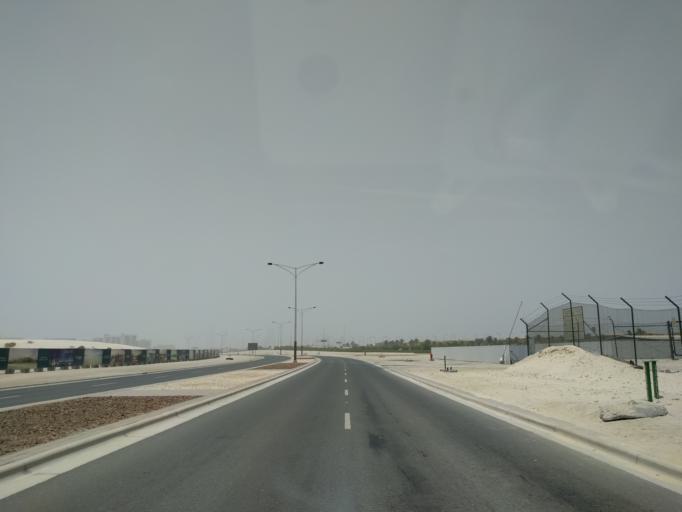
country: AE
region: Abu Dhabi
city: Abu Dhabi
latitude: 24.5396
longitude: 54.4406
